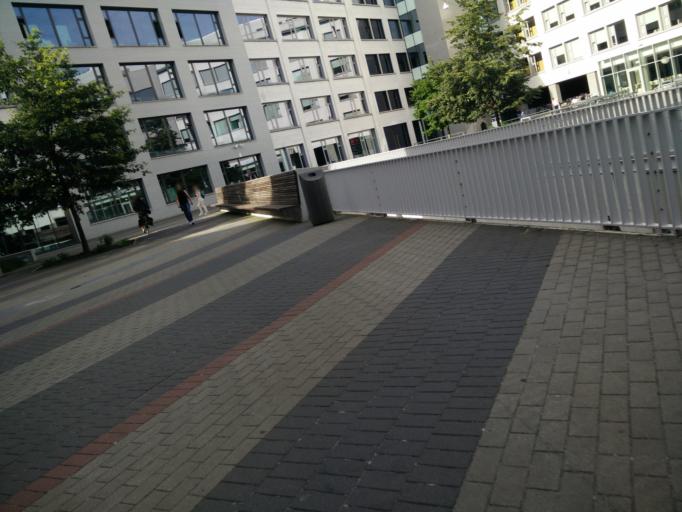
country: BE
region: Flanders
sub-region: Provincie Antwerpen
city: Antwerpen
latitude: 51.2054
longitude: 4.3991
